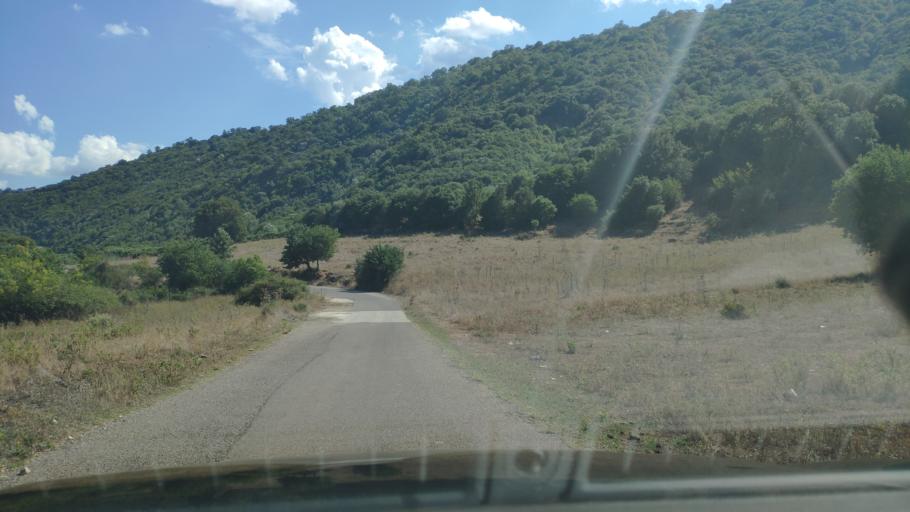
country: GR
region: West Greece
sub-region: Nomos Aitolias kai Akarnanias
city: Katouna
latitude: 38.8336
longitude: 21.0993
